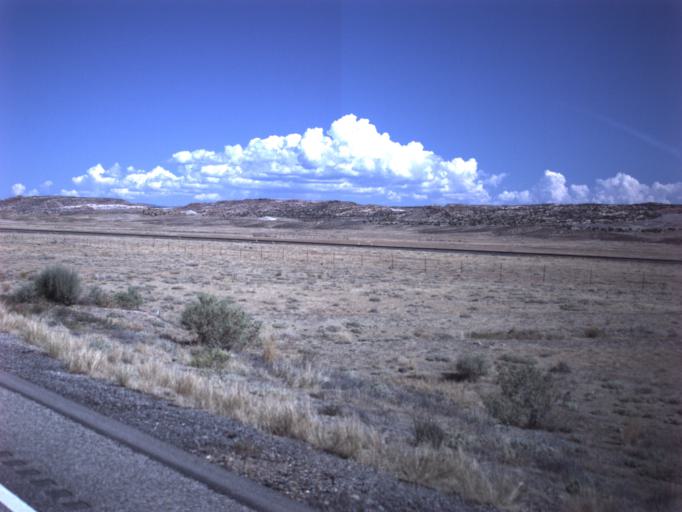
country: US
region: Utah
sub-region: Grand County
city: Moab
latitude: 38.7927
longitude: -109.7578
